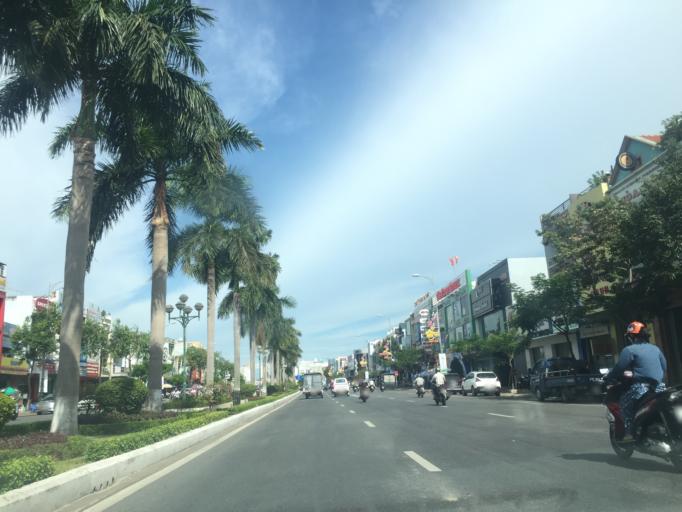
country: VN
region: Da Nang
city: Thanh Khe
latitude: 16.0656
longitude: 108.1967
